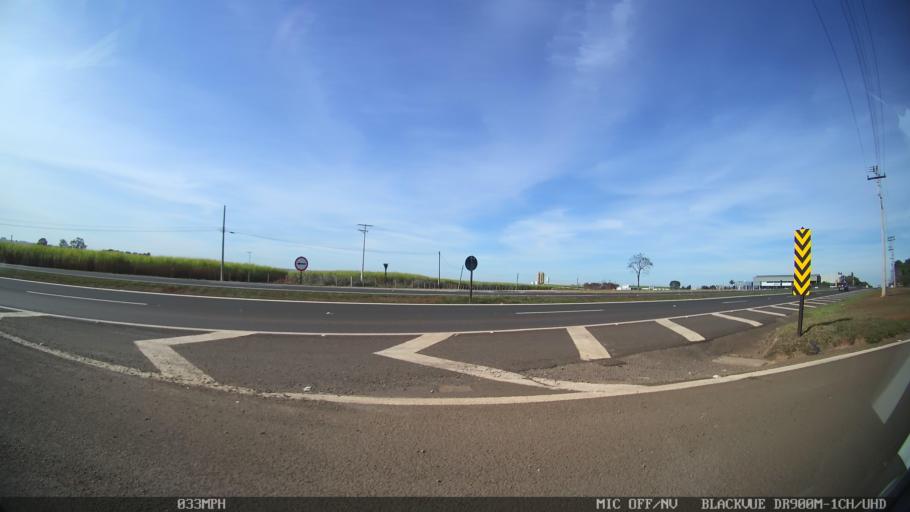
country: BR
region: Sao Paulo
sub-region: Piracicaba
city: Piracicaba
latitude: -22.7801
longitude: -47.6521
